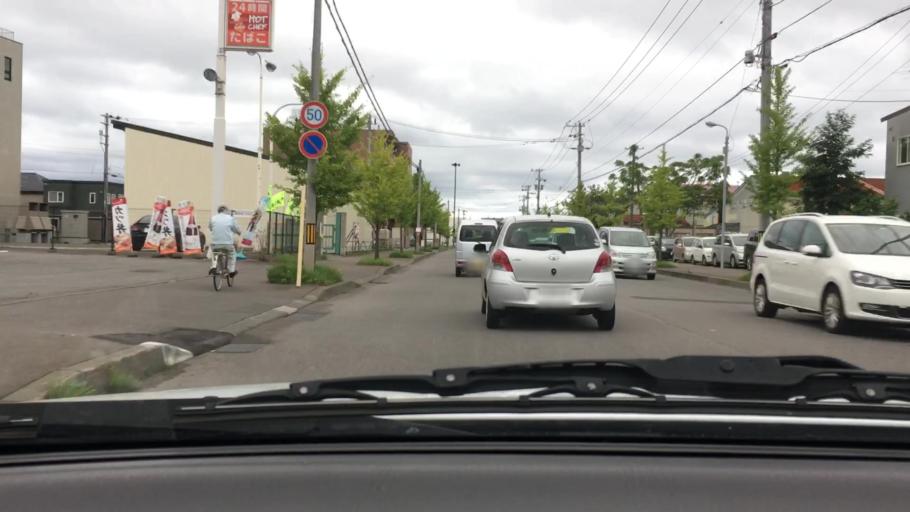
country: JP
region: Hokkaido
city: Hakodate
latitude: 41.7941
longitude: 140.7272
